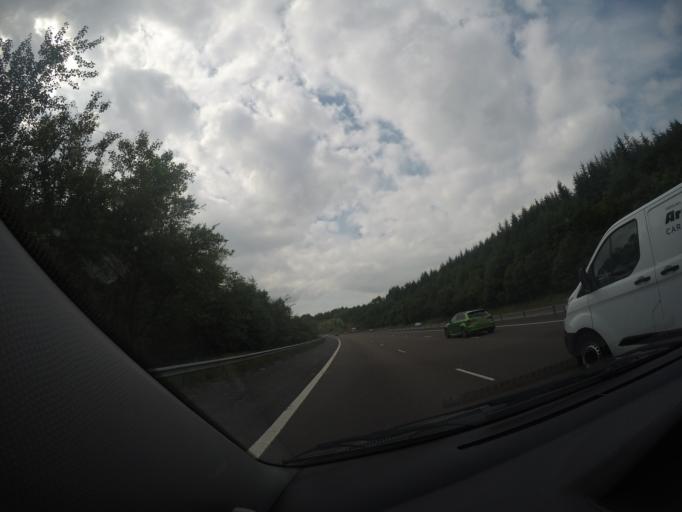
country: GB
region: Scotland
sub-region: Dumfries and Galloway
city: Moffat
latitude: 55.4062
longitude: -3.5584
